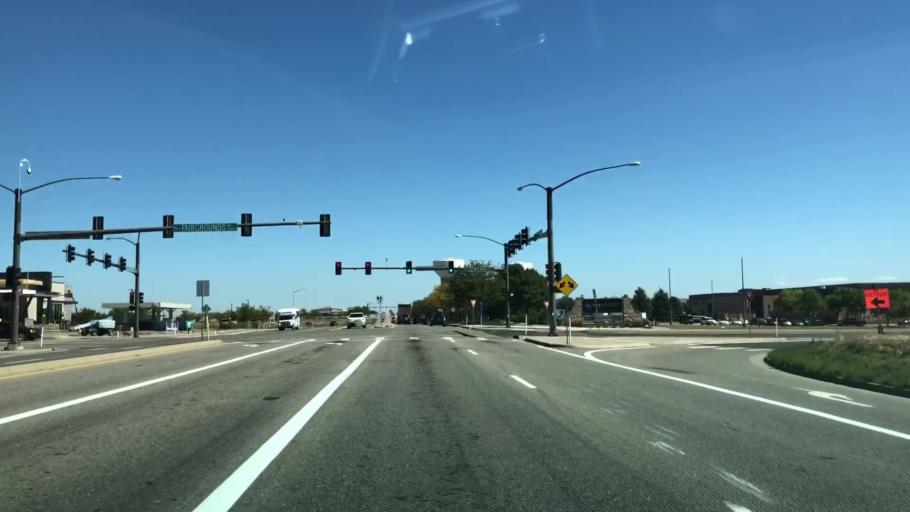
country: US
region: Colorado
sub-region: Weld County
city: Windsor
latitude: 40.4359
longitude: -104.9831
